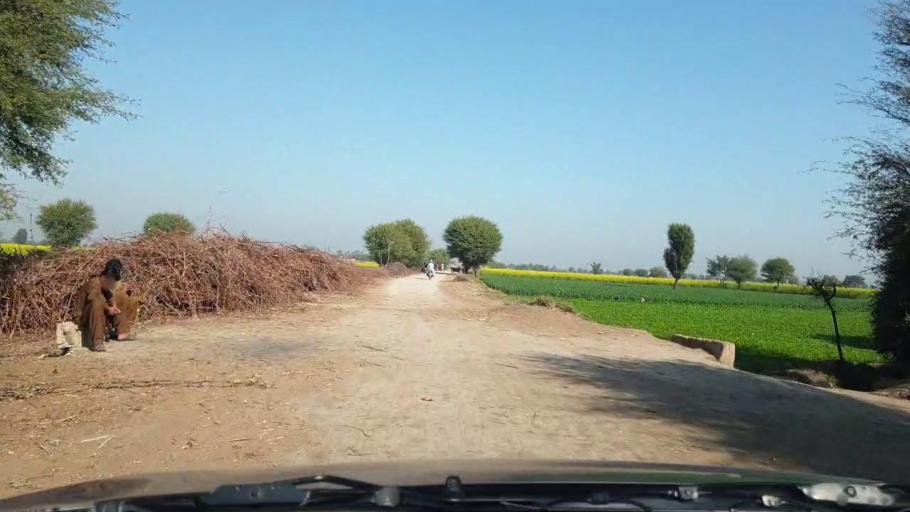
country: PK
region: Sindh
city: Jhol
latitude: 25.9468
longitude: 68.8193
